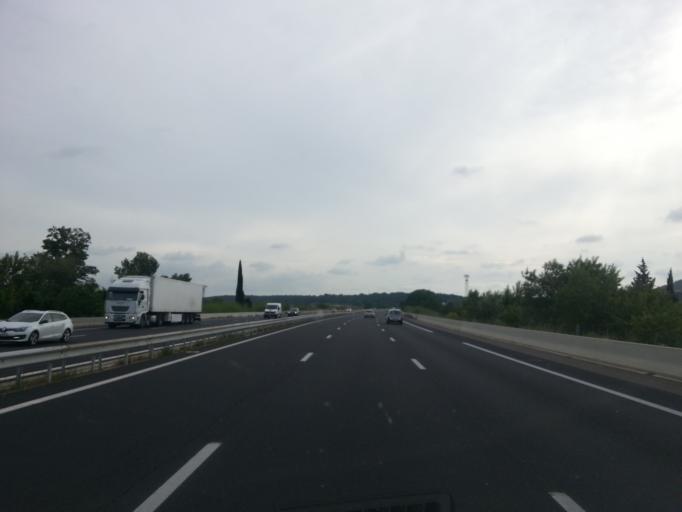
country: FR
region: Languedoc-Roussillon
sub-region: Departement du Gard
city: Sernhac
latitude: 43.9118
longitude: 4.5684
